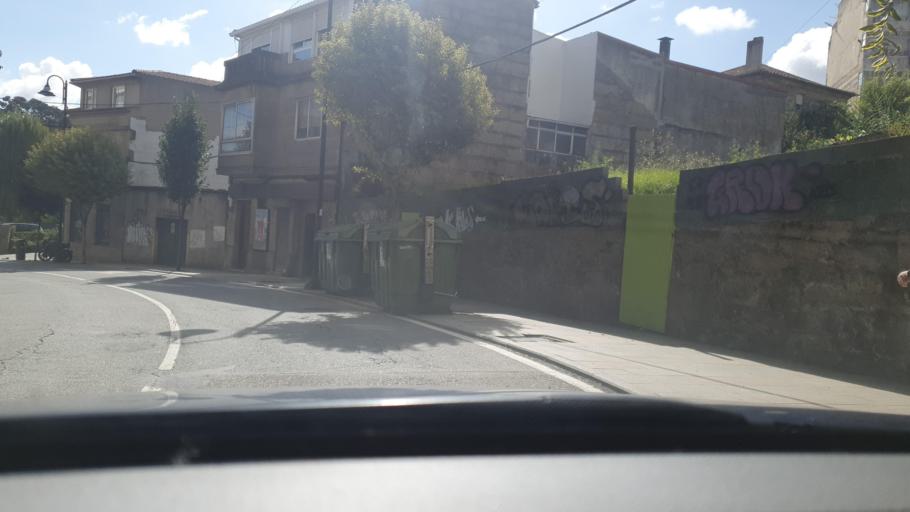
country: ES
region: Galicia
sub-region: Provincia de Pontevedra
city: Vigo
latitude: 42.2242
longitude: -8.7433
